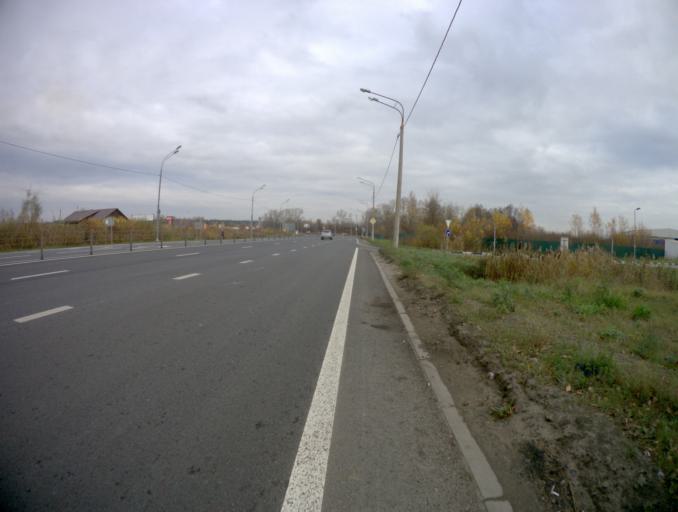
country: RU
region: Moskovskaya
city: Orekhovo-Zuyevo
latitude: 55.8387
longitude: 38.9709
